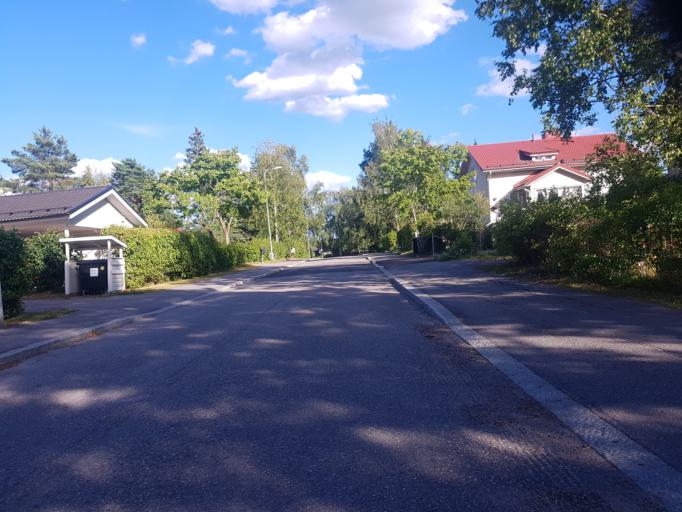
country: FI
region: Uusimaa
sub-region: Helsinki
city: Vantaa
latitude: 60.2847
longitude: 25.0061
